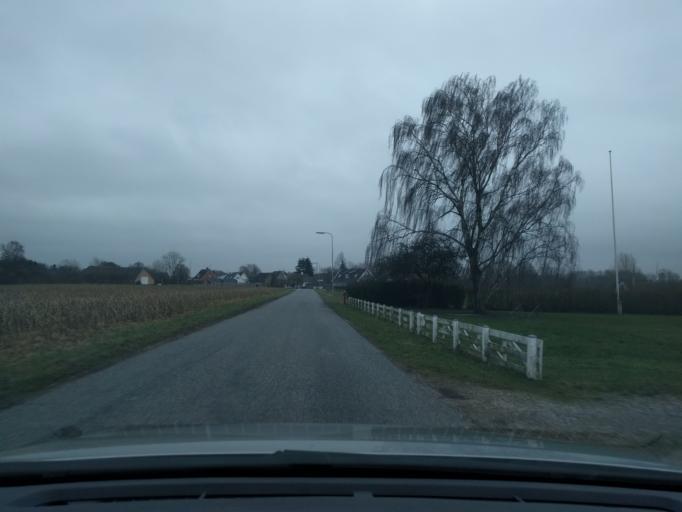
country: DK
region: South Denmark
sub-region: Odense Kommune
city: Neder Holluf
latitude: 55.3765
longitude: 10.5007
